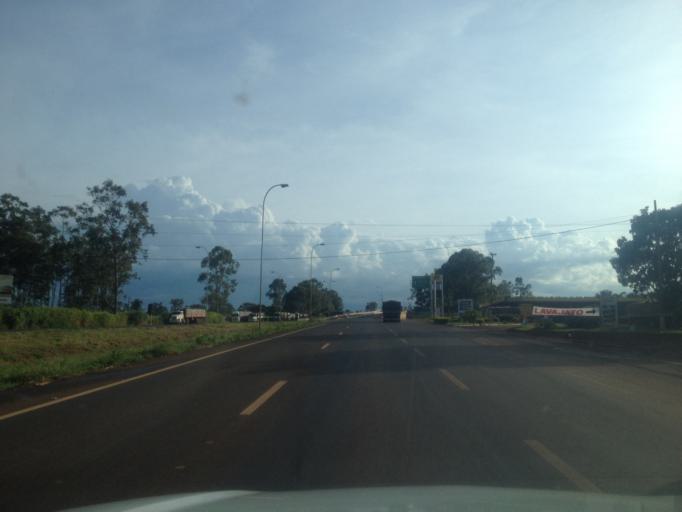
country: BR
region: Goias
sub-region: Jatai
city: Jatai
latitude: -17.9203
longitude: -51.6991
